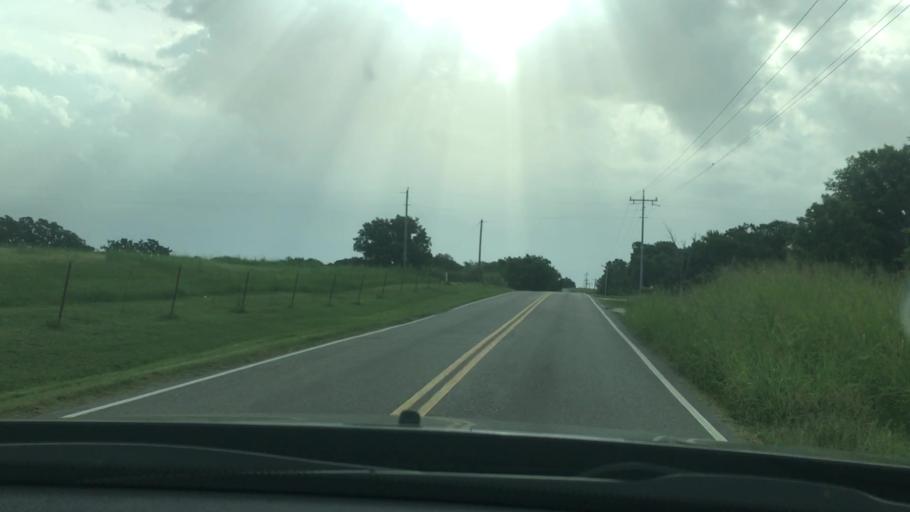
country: US
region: Oklahoma
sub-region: Pontotoc County
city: Ada
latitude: 34.8105
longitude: -96.6222
